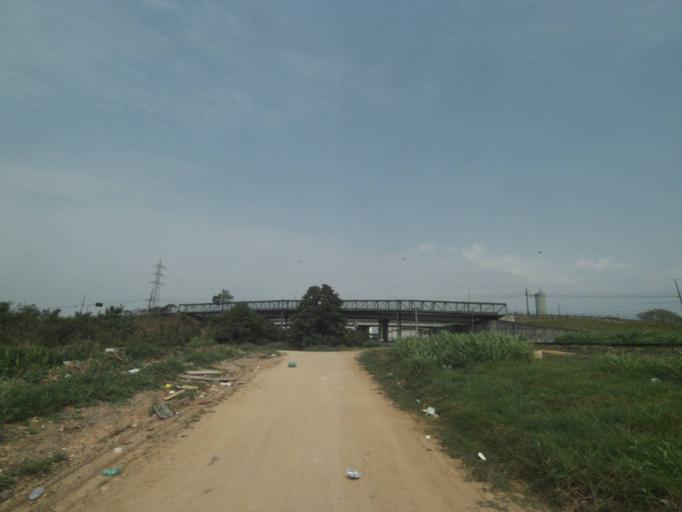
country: BR
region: Parana
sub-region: Sao Jose Dos Pinhais
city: Sao Jose dos Pinhais
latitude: -25.5004
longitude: -49.2078
